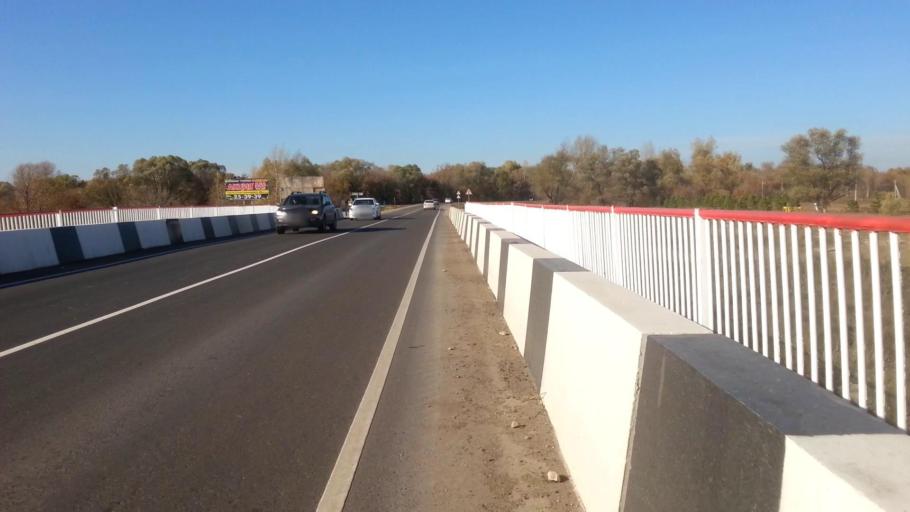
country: RU
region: Altai Krai
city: Sannikovo
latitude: 53.3198
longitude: 83.9442
